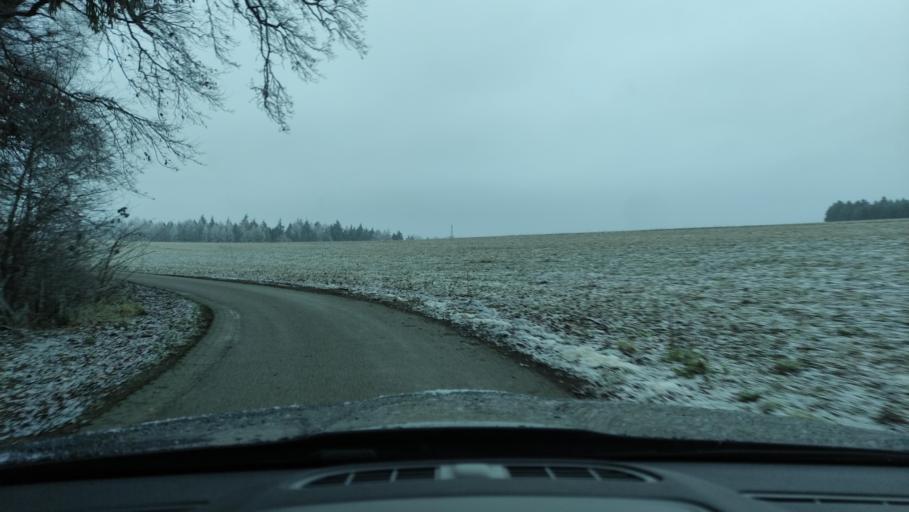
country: DE
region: Bavaria
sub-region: Swabia
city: Deisenhausen
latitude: 48.2640
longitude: 10.3399
